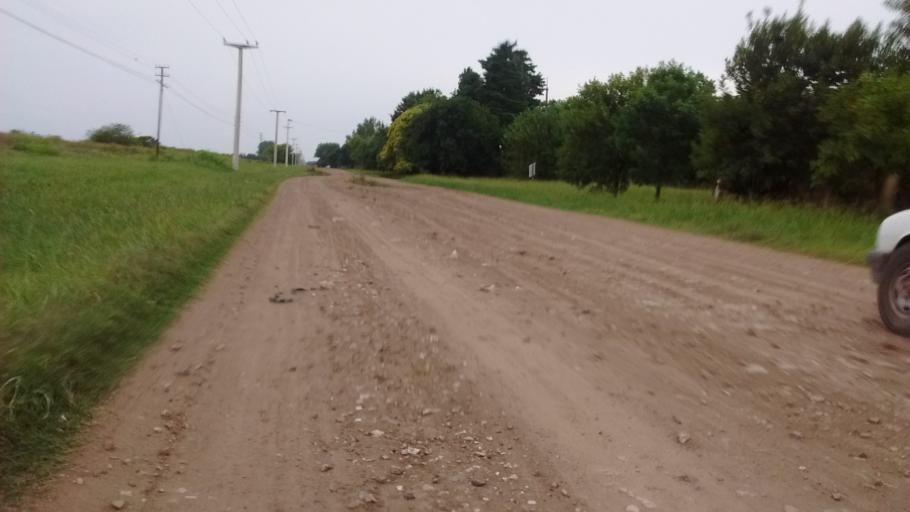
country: AR
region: Santa Fe
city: Funes
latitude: -32.9125
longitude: -60.8372
